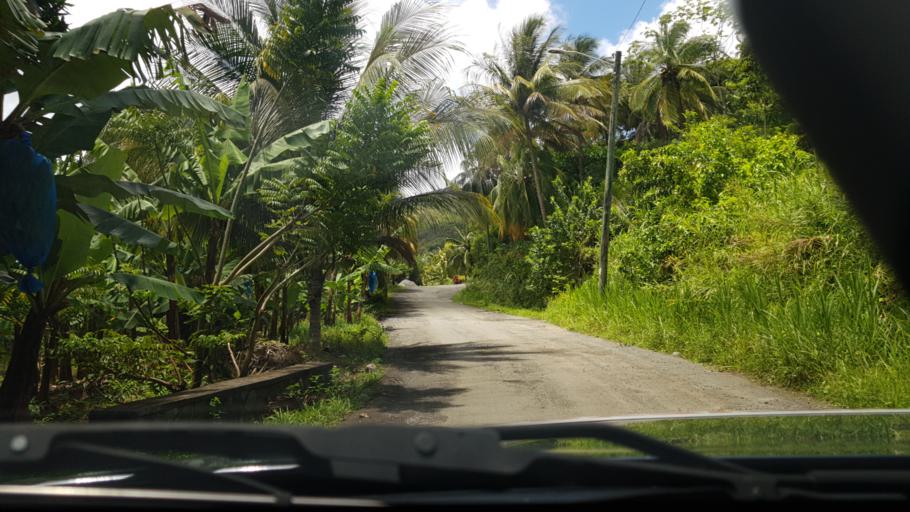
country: LC
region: Anse-la-Raye
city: Anse La Raye
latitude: 13.9527
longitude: -60.9999
